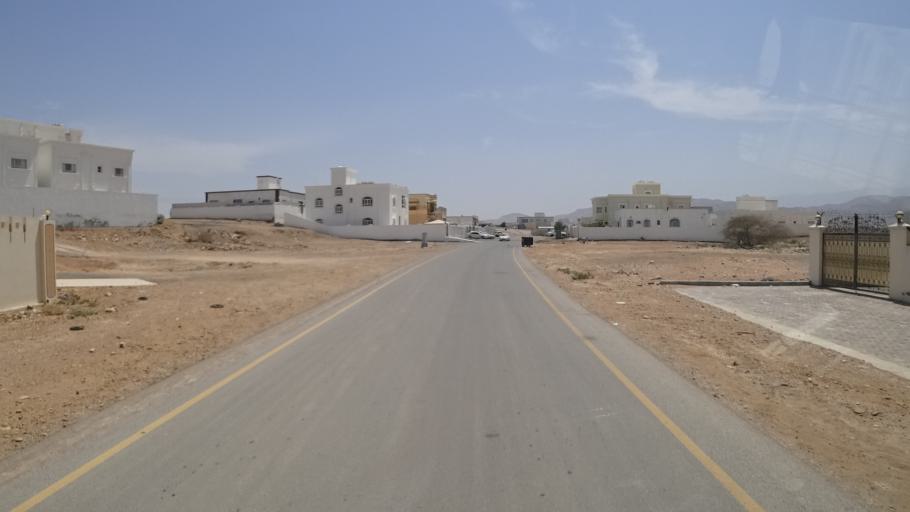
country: OM
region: Ash Sharqiyah
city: Sur
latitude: 22.6082
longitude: 59.4679
